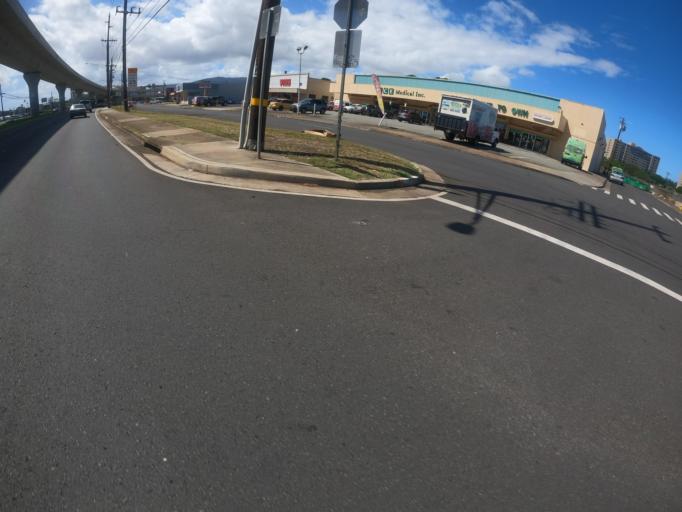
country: US
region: Hawaii
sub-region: Honolulu County
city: Waipahu
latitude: 21.3850
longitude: -158.0010
